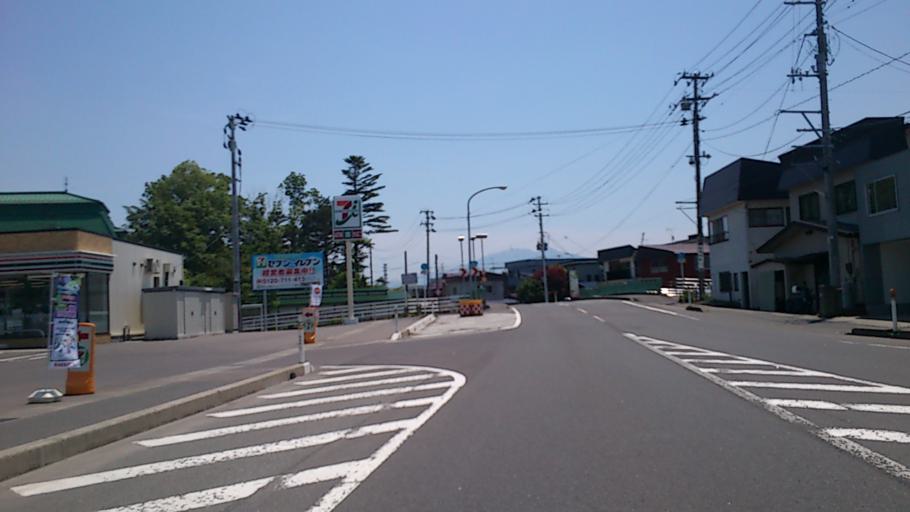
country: JP
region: Aomori
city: Aomori Shi
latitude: 40.8321
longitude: 140.7243
